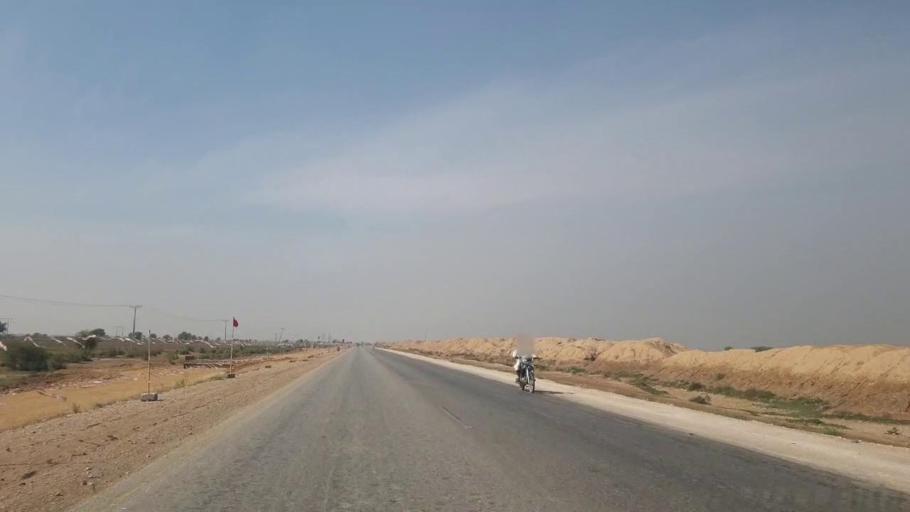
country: PK
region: Sindh
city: Sann
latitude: 26.0046
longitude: 68.1568
